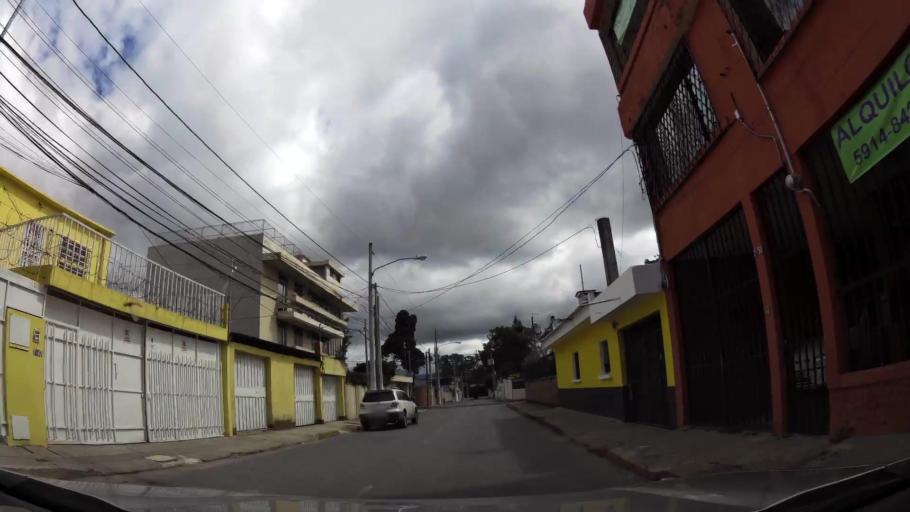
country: GT
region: Guatemala
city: Guatemala City
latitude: 14.6104
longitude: -90.5083
